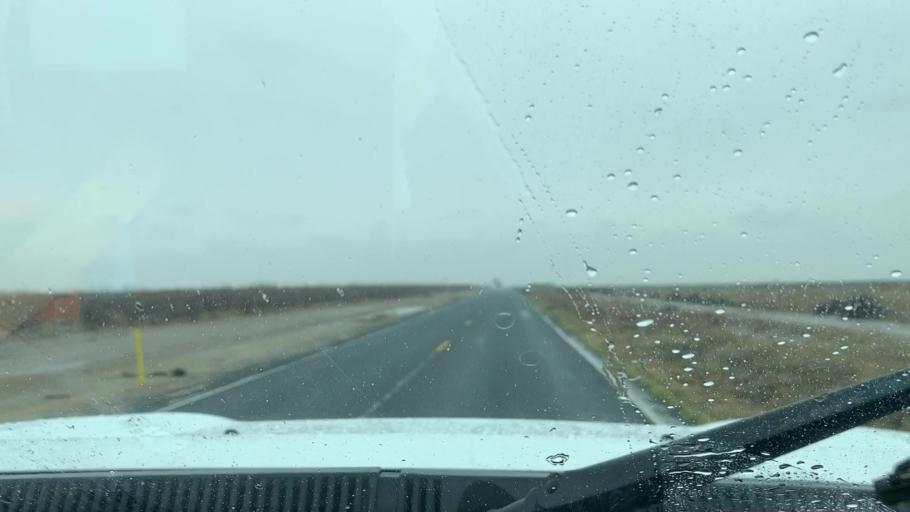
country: US
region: California
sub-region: Tulare County
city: Earlimart
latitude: 35.8918
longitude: -119.3643
